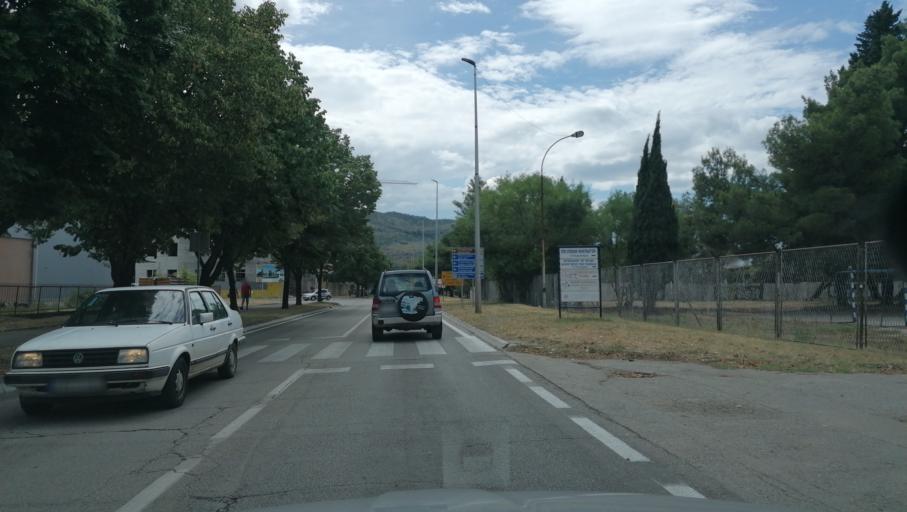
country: BA
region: Republika Srpska
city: Trebinje
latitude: 42.7087
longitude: 18.3425
